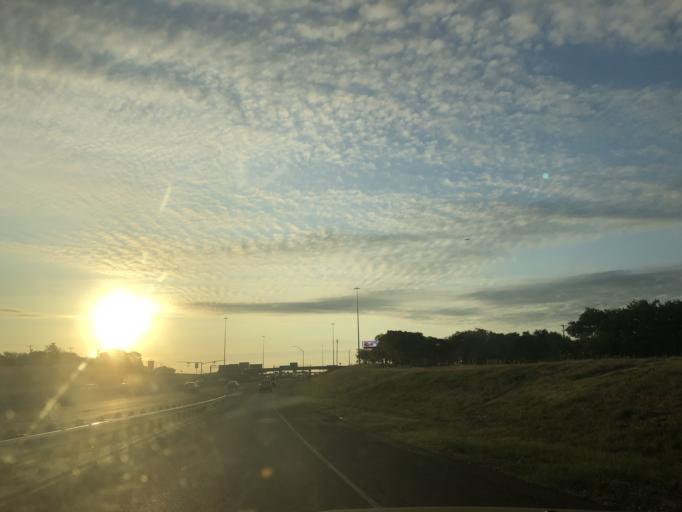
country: US
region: Texas
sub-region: Tarrant County
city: Euless
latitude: 32.8383
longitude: -97.0811
